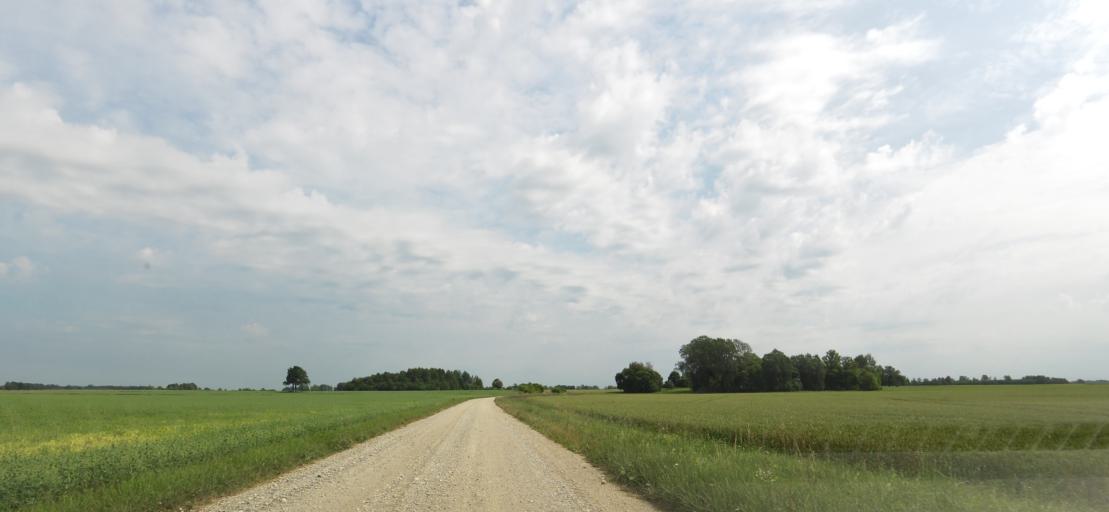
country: LT
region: Panevezys
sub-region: Birzai
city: Birzai
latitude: 56.3200
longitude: 24.6888
